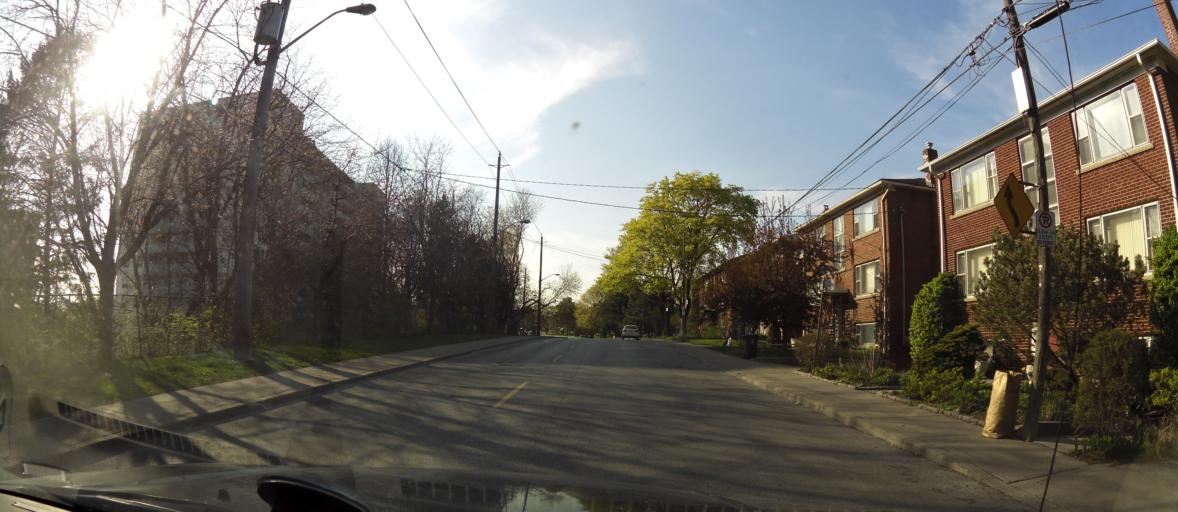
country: CA
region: Ontario
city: Toronto
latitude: 43.6395
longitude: -79.4723
